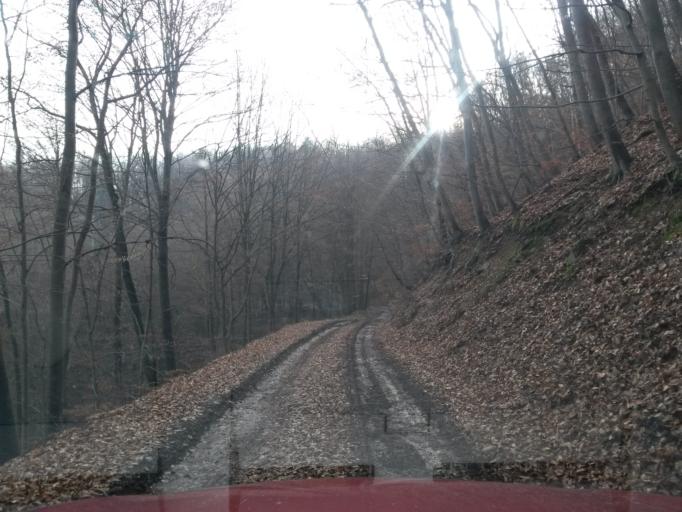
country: SK
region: Kosicky
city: Dobsina
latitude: 48.7436
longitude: 20.4056
